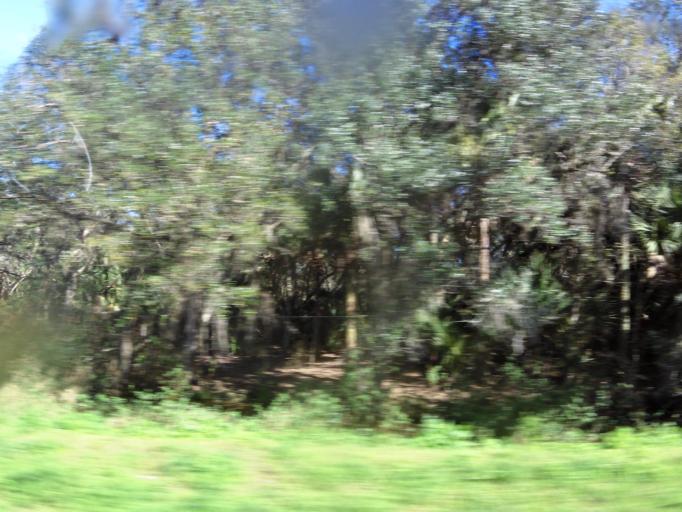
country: US
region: Florida
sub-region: Brevard County
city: Port Saint John
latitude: 28.5373
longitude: -80.8064
